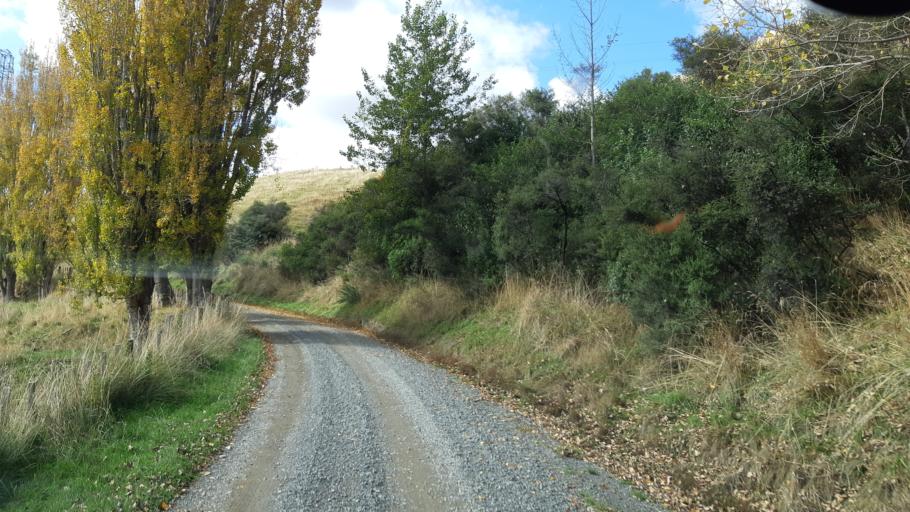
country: NZ
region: Manawatu-Wanganui
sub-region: Ruapehu District
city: Waiouru
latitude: -39.7670
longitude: 175.6713
